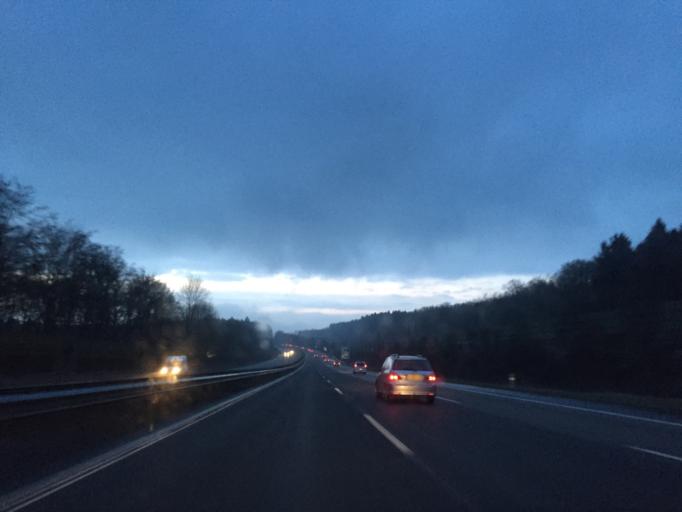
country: DE
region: Rheinland-Pfalz
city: Dernbach
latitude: 50.5422
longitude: 7.5896
